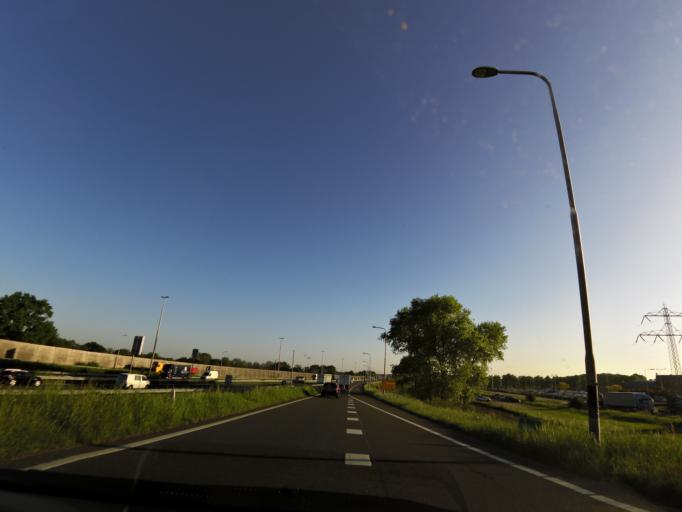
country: NL
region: Limburg
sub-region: Gemeente Sittard-Geleen
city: Born
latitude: 51.0409
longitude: 5.8261
